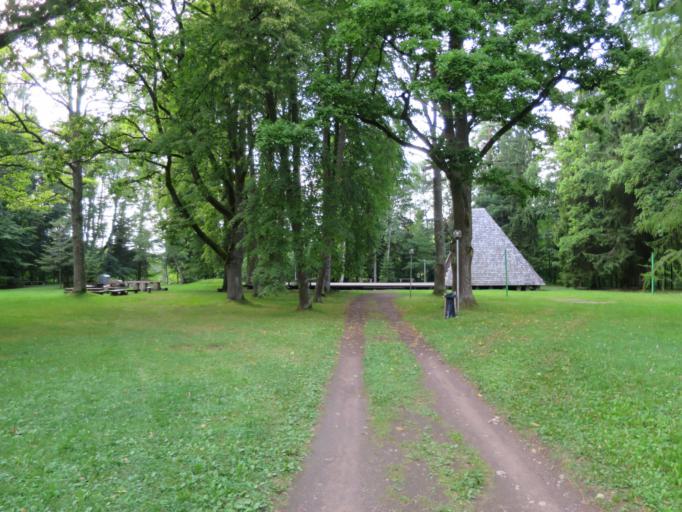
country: LV
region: Priekuli
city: Priekuli
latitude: 57.2865
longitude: 25.4679
